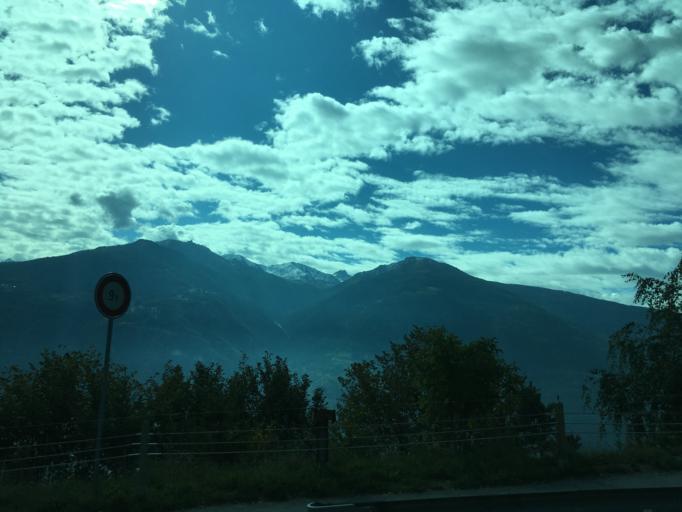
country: CH
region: Valais
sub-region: Sierre District
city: Chermignon-d'en Haut
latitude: 46.2851
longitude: 7.4767
